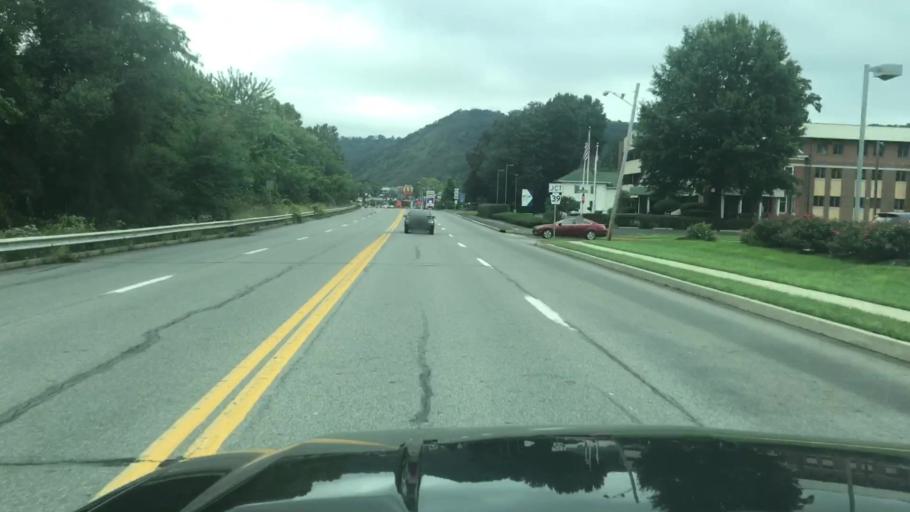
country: US
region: Pennsylvania
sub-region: Perry County
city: Marysville
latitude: 40.3217
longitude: -76.8987
